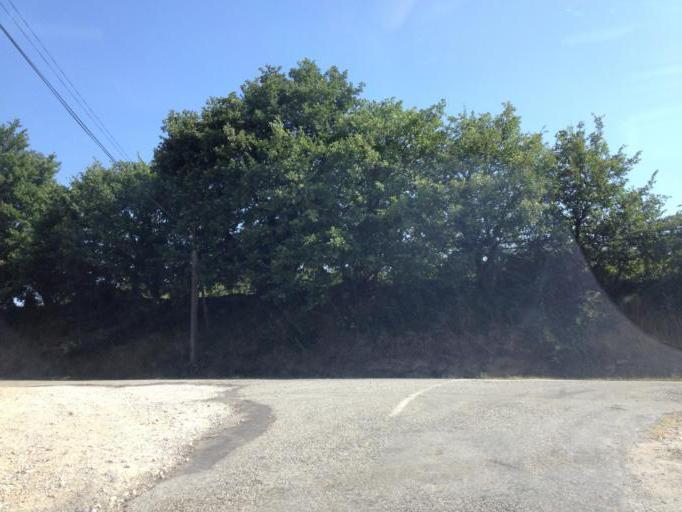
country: FR
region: Rhone-Alpes
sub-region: Departement de la Drome
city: Clerieux
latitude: 45.1384
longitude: 4.9432
